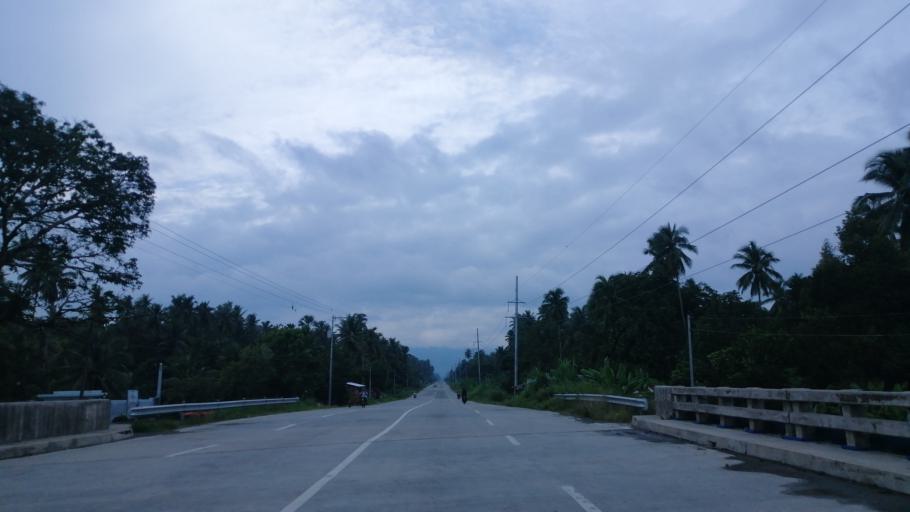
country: PH
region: Davao
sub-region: Province of Davao del Norte
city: Corocotan
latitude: 7.3956
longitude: 125.7811
